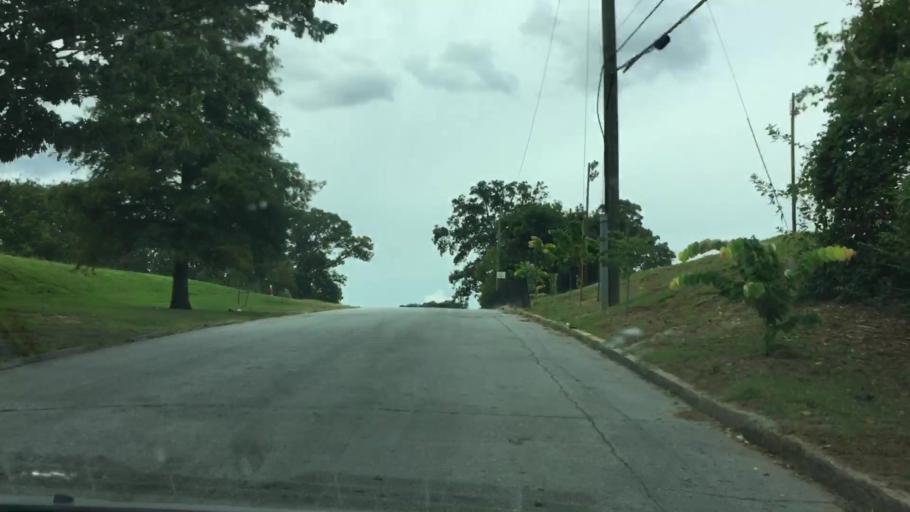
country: US
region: Georgia
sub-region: Fulton County
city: Atlanta
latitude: 33.7698
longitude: -84.4255
